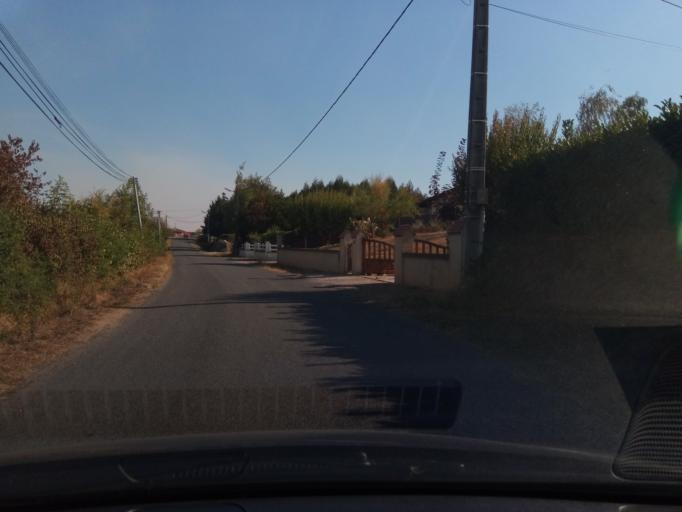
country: FR
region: Poitou-Charentes
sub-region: Departement de la Vienne
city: Montmorillon
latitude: 46.4173
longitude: 0.8723
